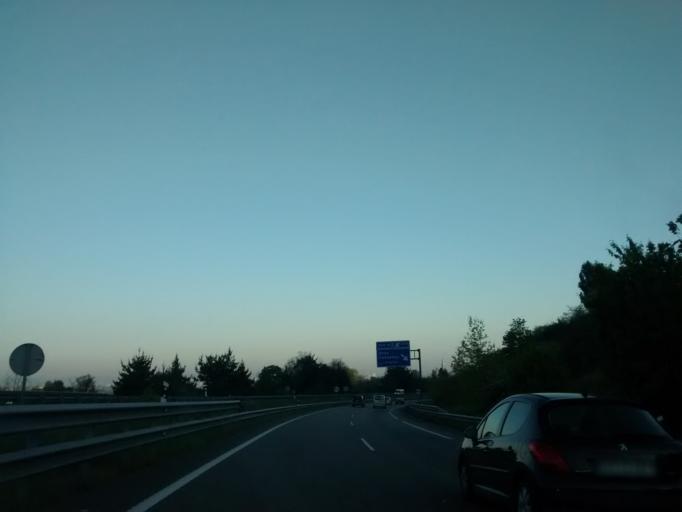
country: ES
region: Asturias
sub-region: Province of Asturias
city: Arriba
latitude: 43.5045
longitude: -5.5922
